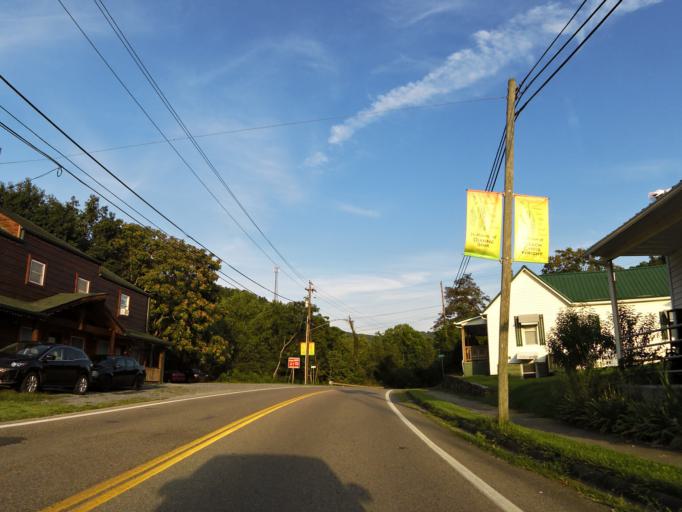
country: US
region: Virginia
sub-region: Washington County
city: Emory
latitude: 36.6403
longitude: -81.7971
